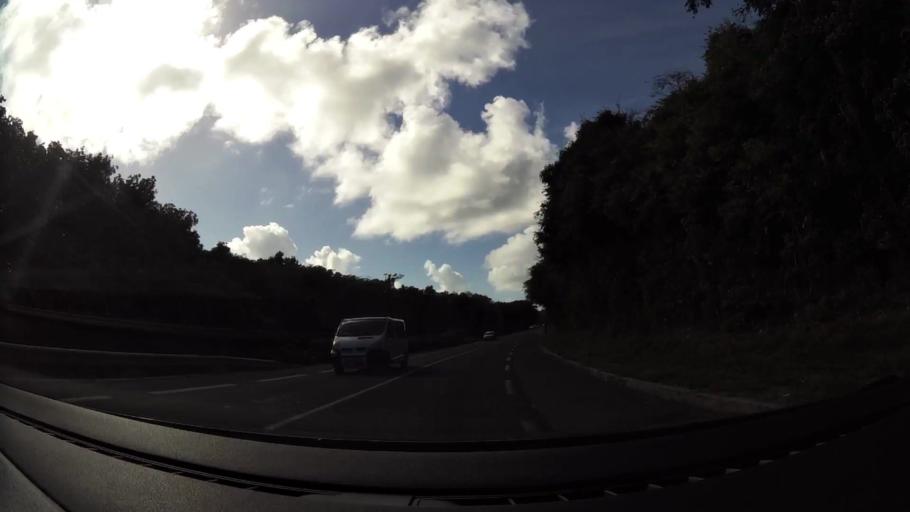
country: GP
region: Guadeloupe
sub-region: Guadeloupe
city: Le Gosier
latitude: 16.2072
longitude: -61.4435
